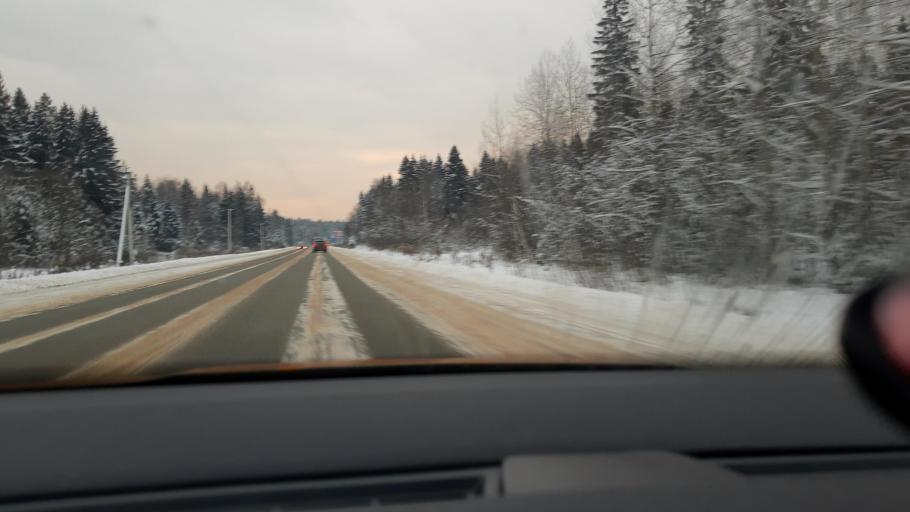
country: RU
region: Moskovskaya
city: Yershovo
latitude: 55.8031
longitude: 36.9491
